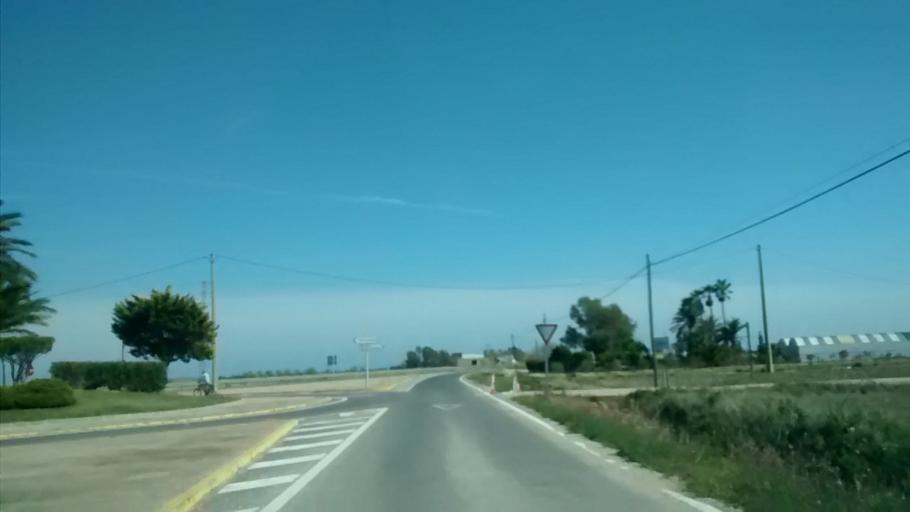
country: ES
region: Catalonia
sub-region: Provincia de Tarragona
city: Deltebre
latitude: 40.7118
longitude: 0.7557
